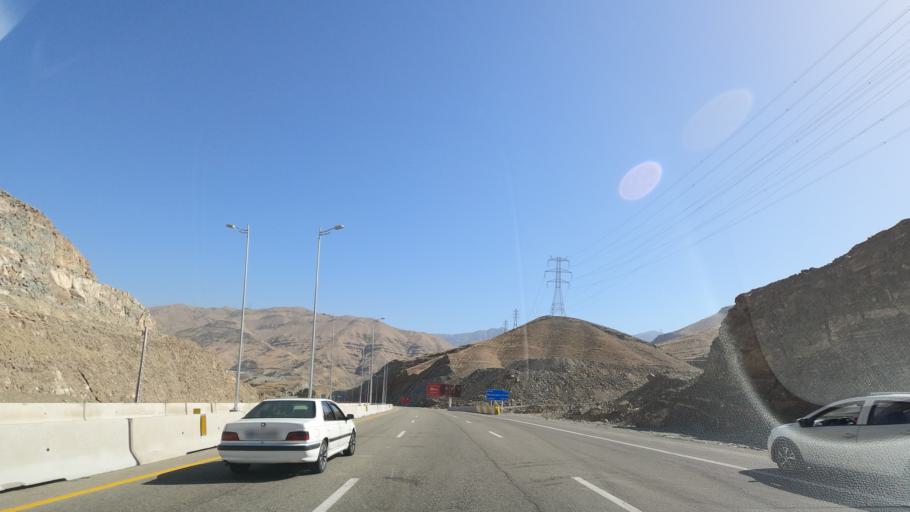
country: IR
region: Alborz
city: Karaj
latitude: 35.8143
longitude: 51.0373
